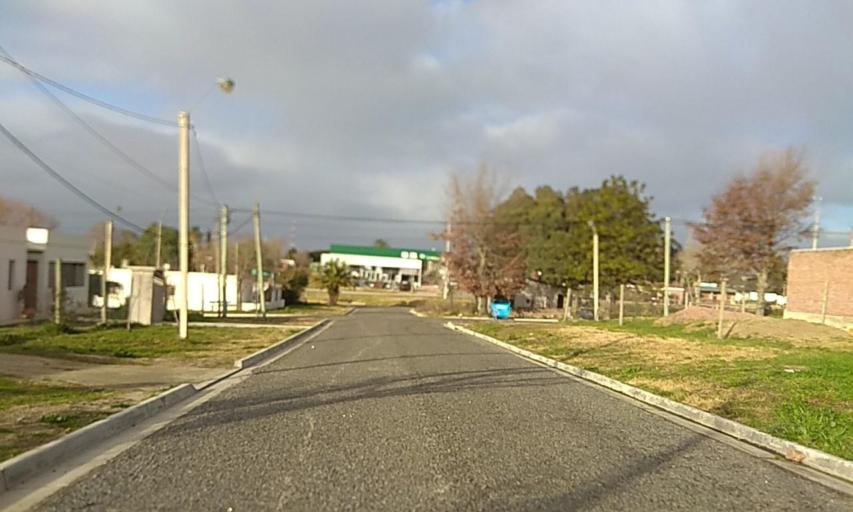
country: UY
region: Florida
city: Florida
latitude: -34.0843
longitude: -56.2114
